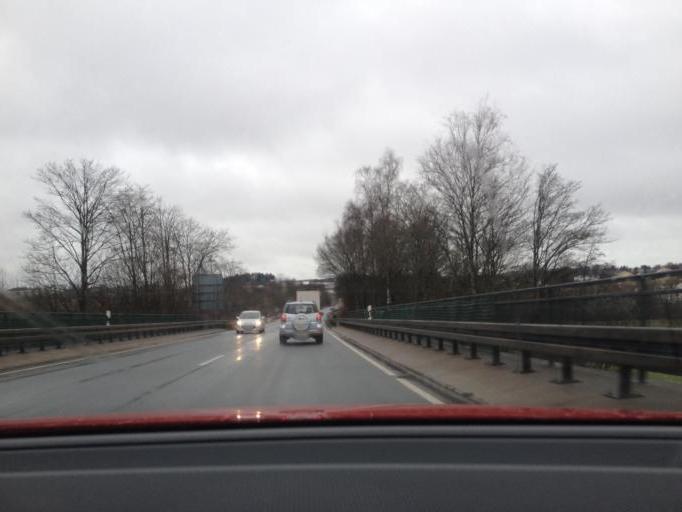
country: DE
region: Bavaria
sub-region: Upper Franconia
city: Dohlau
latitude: 50.2850
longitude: 11.9373
